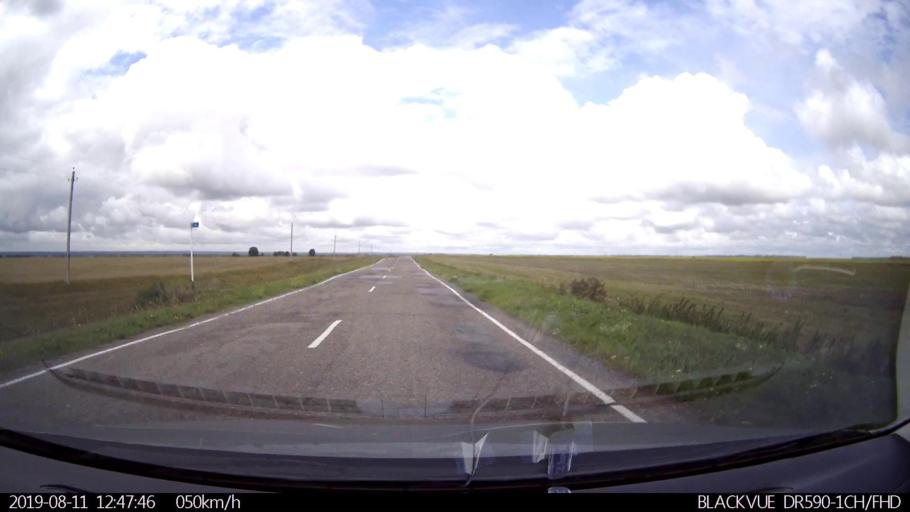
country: RU
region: Ulyanovsk
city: Ignatovka
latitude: 53.8709
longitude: 47.7056
